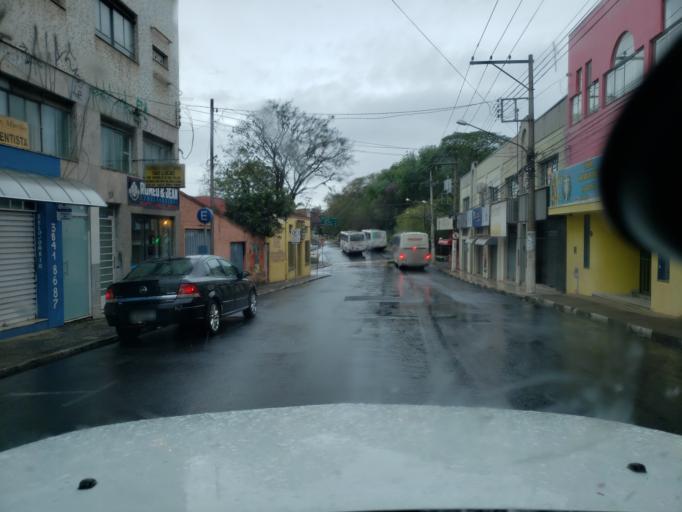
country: BR
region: Sao Paulo
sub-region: Moji-Guacu
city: Mogi-Gaucu
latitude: -22.3731
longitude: -46.9420
